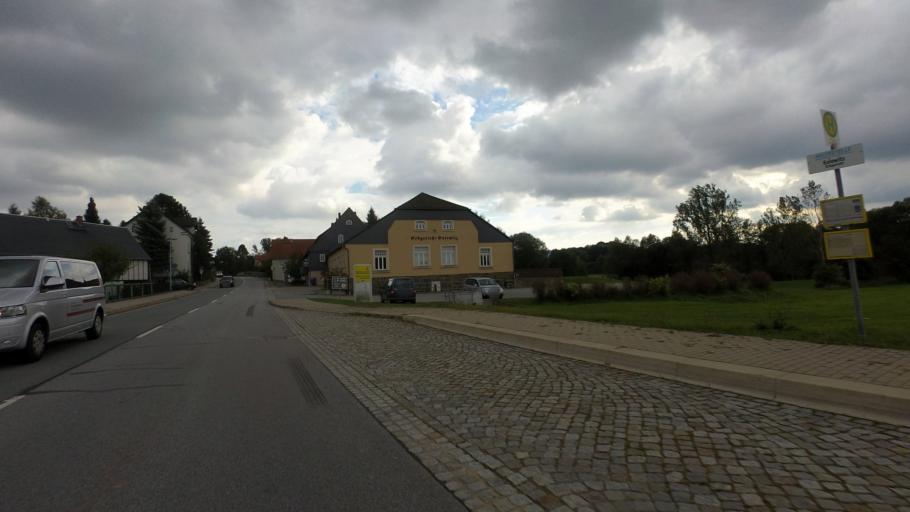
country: DE
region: Saxony
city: Grosspostwitz
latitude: 51.1122
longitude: 14.4545
